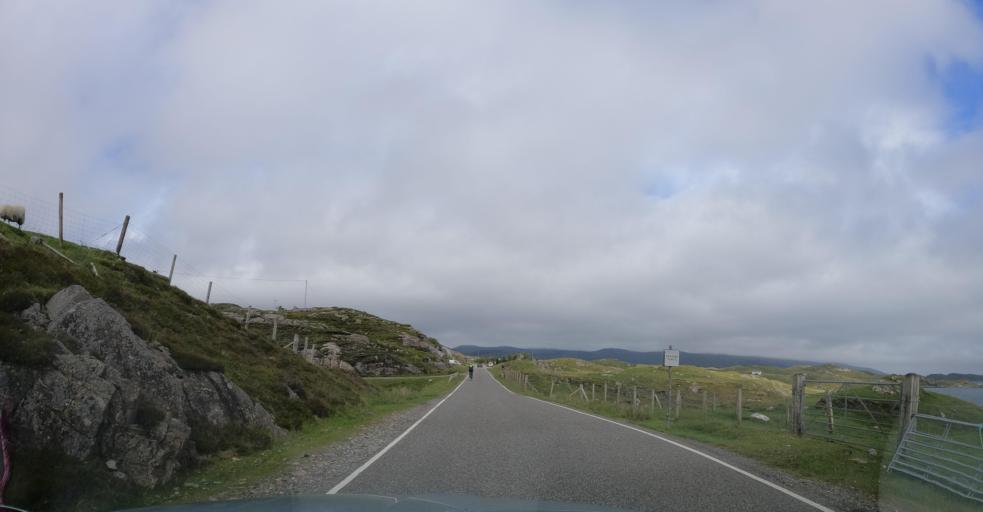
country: GB
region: Scotland
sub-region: Eilean Siar
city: Harris
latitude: 57.8822
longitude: -6.8150
